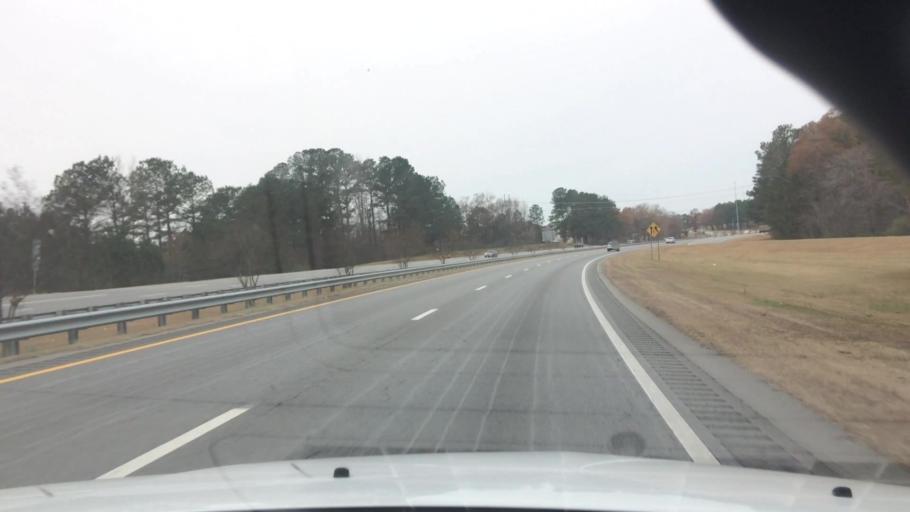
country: US
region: North Carolina
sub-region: Nash County
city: Rocky Mount
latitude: 35.9712
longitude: -77.8393
